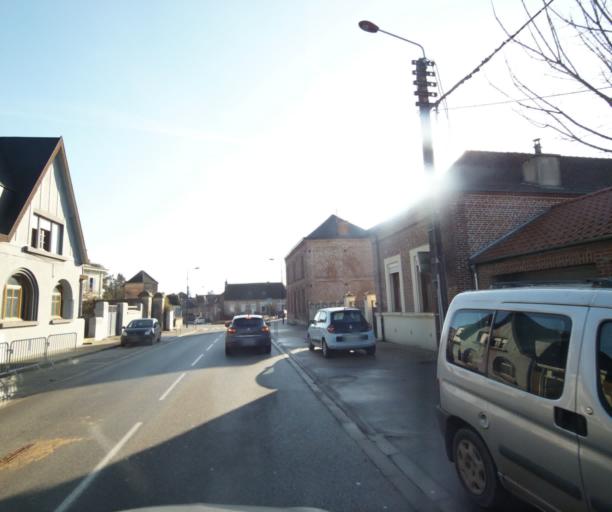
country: FR
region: Nord-Pas-de-Calais
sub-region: Departement du Nord
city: Preseau
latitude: 50.3126
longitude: 3.5759
